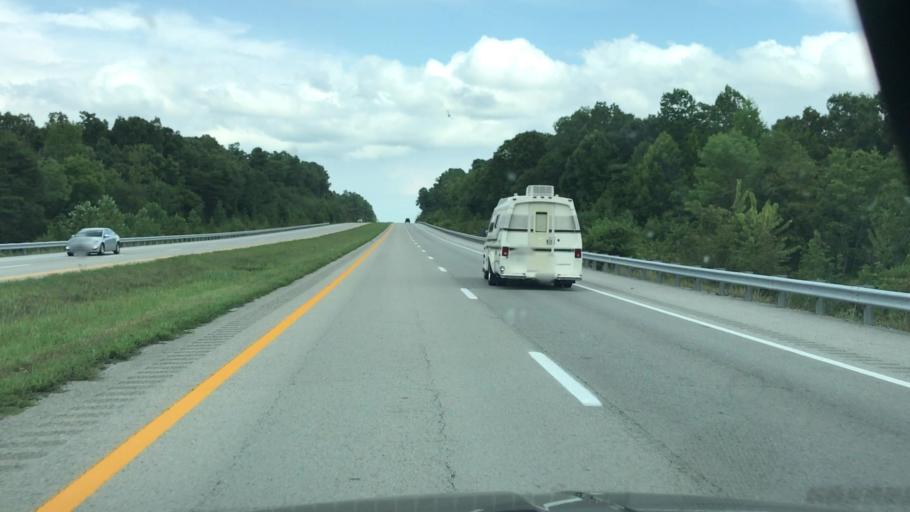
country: US
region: Kentucky
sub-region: Hopkins County
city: Dawson Springs
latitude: 37.1954
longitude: -87.6399
